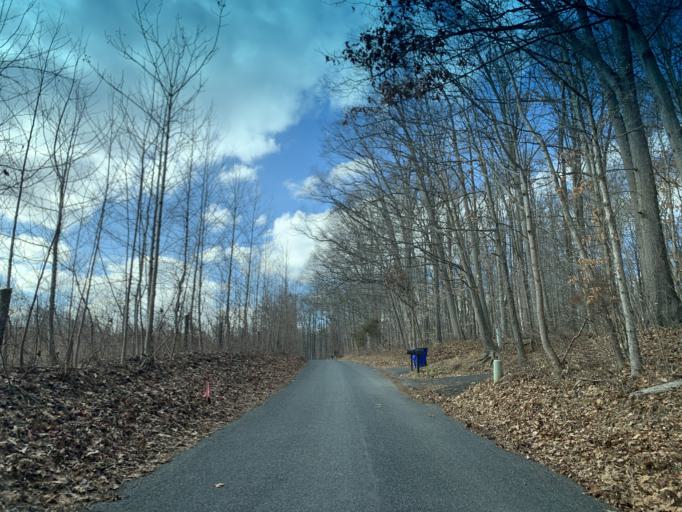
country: US
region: Maryland
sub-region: Harford County
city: Riverside
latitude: 39.5061
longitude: -76.2623
